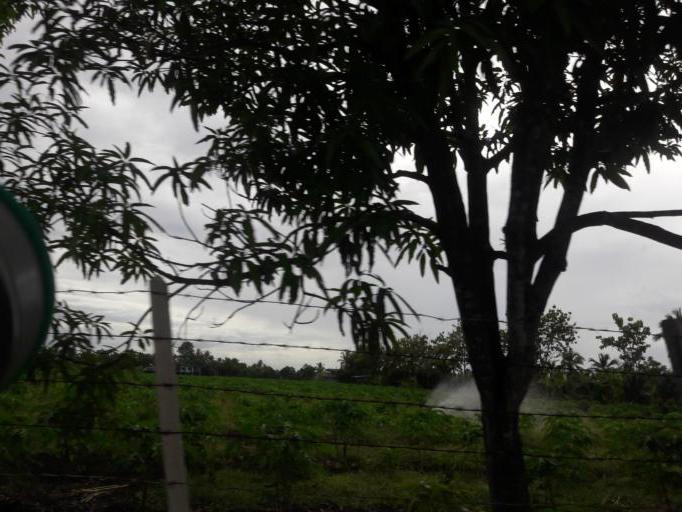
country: TH
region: Ratchaburi
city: Damnoen Saduak
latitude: 13.5363
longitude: 100.0122
